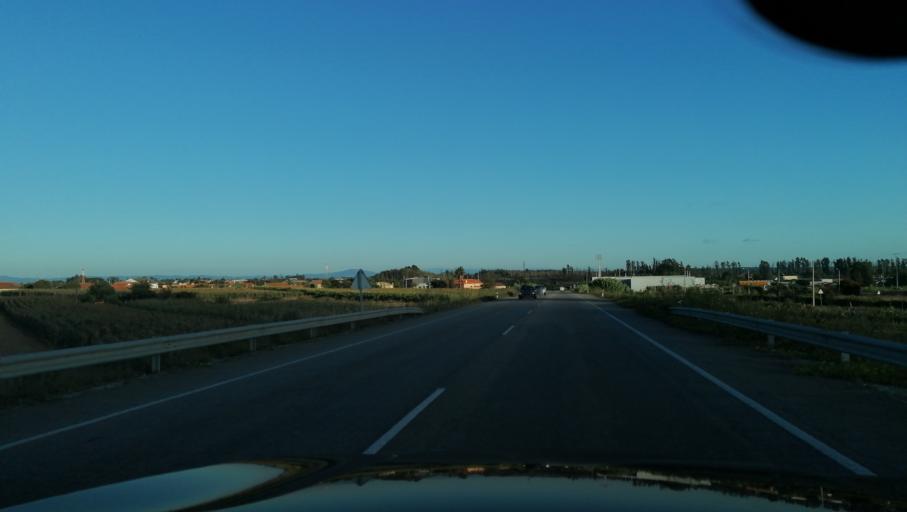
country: PT
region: Aveiro
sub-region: Aveiro
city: Oliveirinha
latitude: 40.5892
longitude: -8.6086
